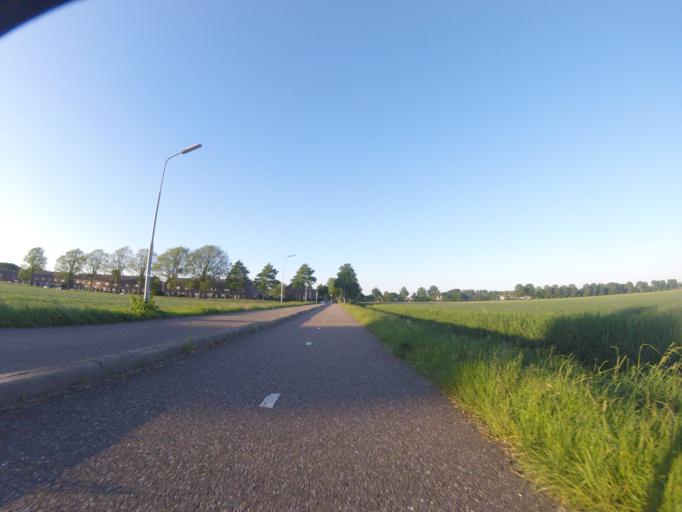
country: NL
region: North Holland
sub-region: Gemeente Haarlemmermeer
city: Hoofddorp
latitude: 52.3755
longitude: 4.7333
